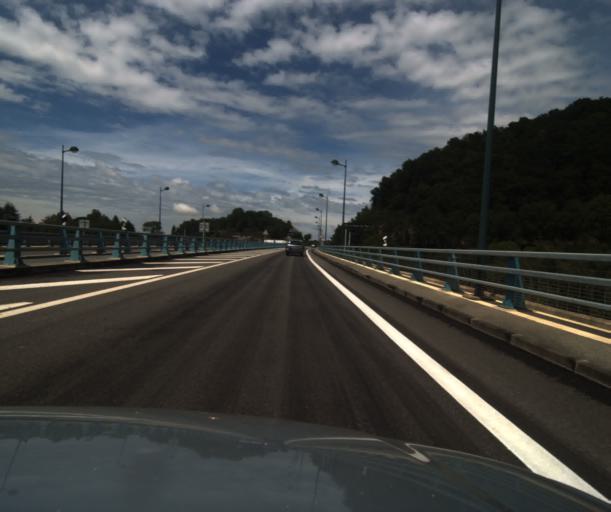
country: FR
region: Midi-Pyrenees
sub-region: Departement des Hautes-Pyrenees
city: Lourdes
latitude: 43.0812
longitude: -0.0447
